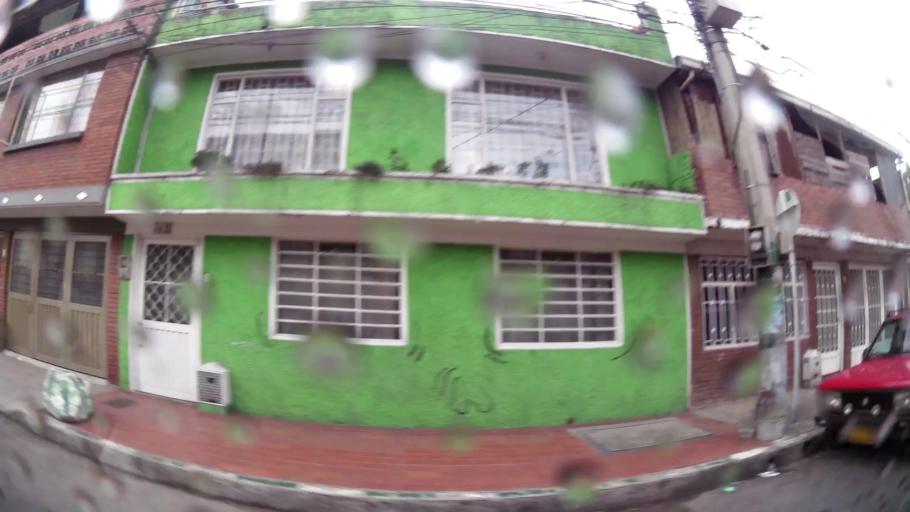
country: CO
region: Bogota D.C.
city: Barrio San Luis
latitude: 4.6961
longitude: -74.0951
